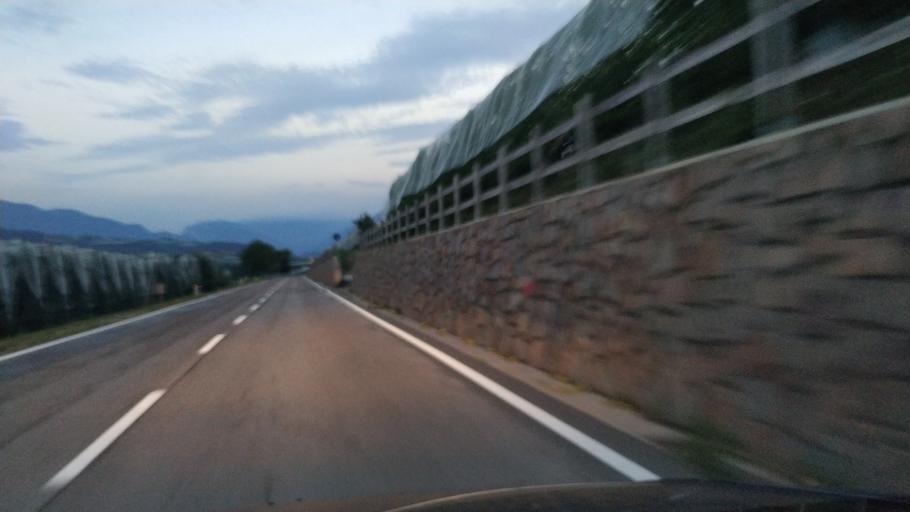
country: IT
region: Trentino-Alto Adige
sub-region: Provincia di Trento
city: Cloz
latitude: 46.4090
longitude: 11.0772
